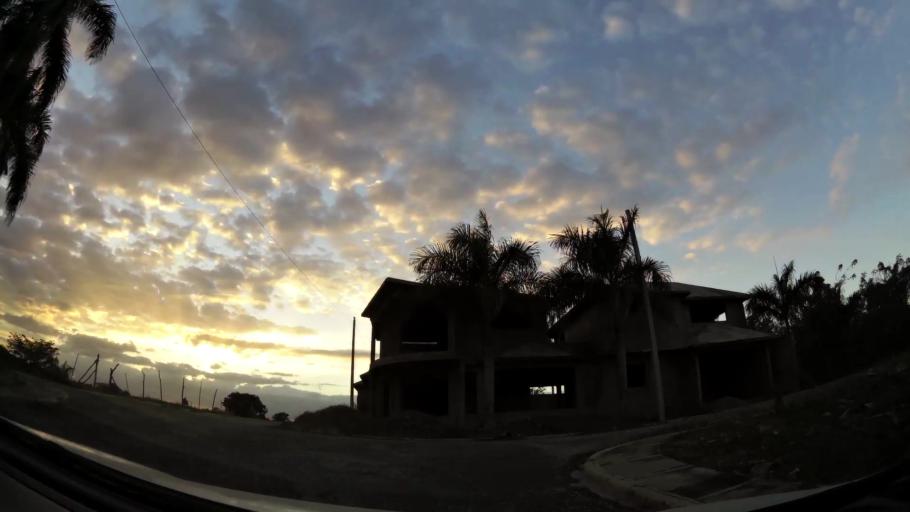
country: DO
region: Nacional
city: La Agustina
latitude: 18.5680
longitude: -69.9432
